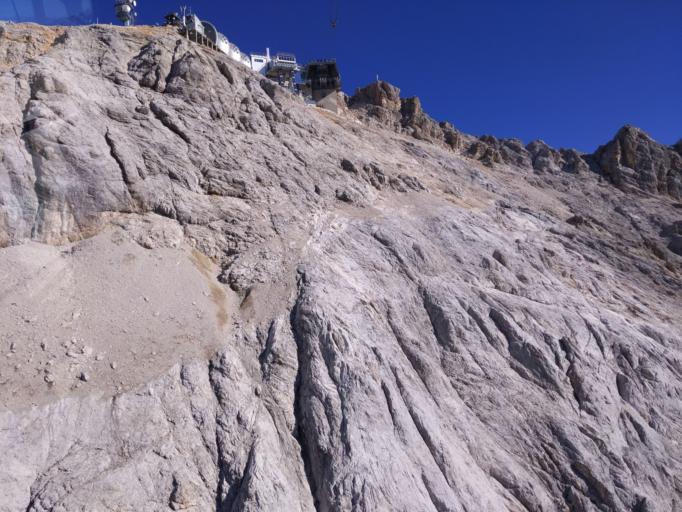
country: DE
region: Bavaria
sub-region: Upper Bavaria
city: Grainau
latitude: 47.4189
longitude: 10.9841
